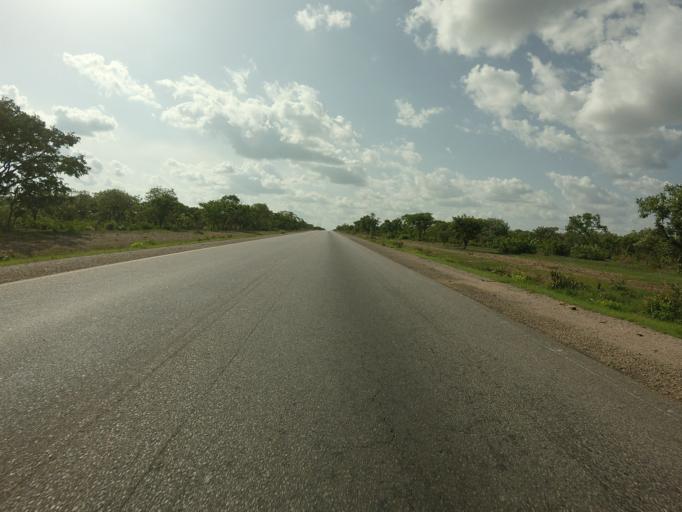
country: GH
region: Upper East
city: Bolgatanga
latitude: 10.5351
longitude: -0.8206
